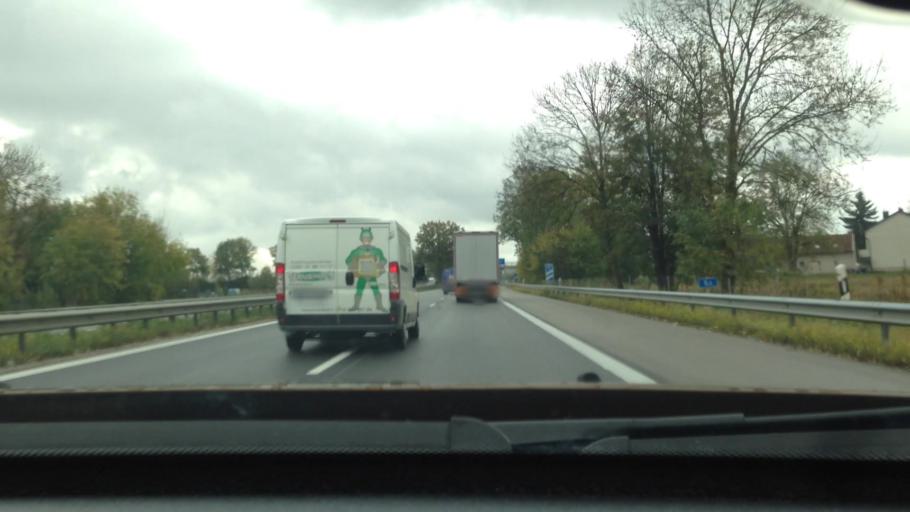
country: DE
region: Bavaria
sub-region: Upper Bavaria
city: Grobenzell
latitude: 48.1988
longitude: 11.4058
